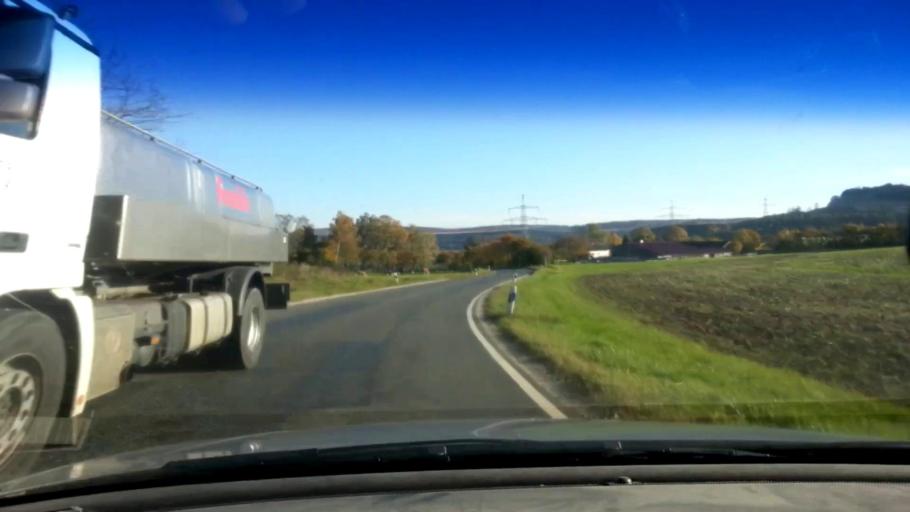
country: DE
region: Bavaria
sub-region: Upper Franconia
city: Poxdorf
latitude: 49.8942
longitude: 11.1017
